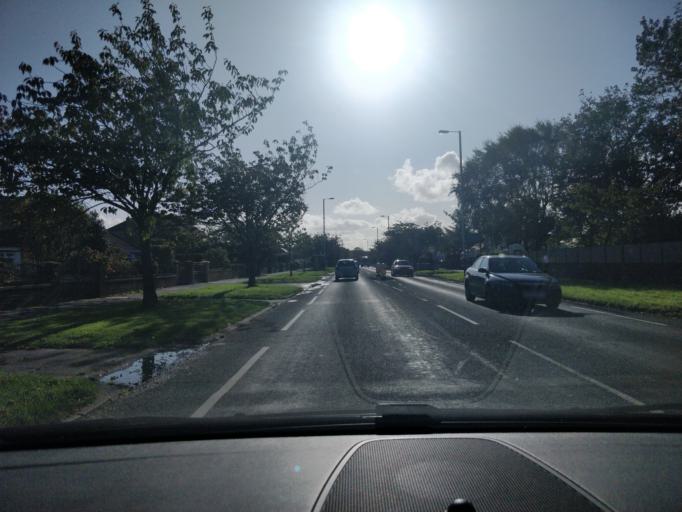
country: GB
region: England
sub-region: Lancashire
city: Banks
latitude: 53.6739
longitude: -2.9535
